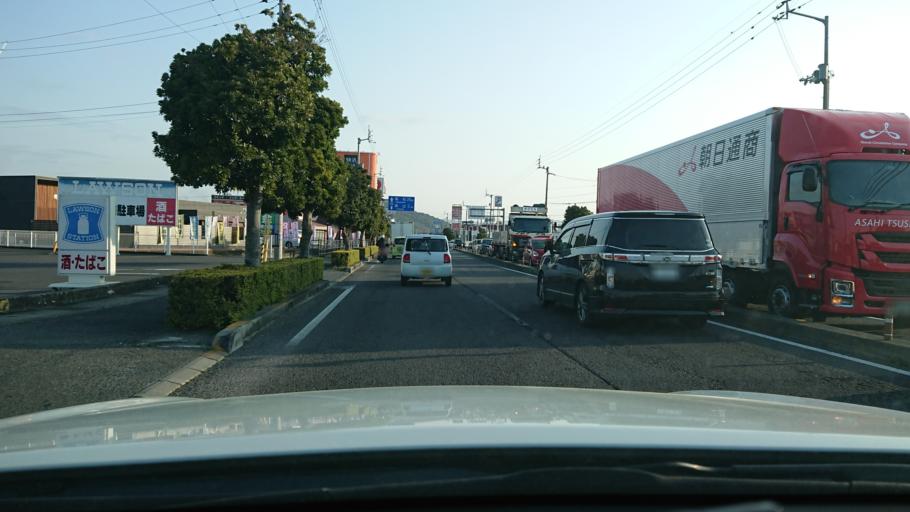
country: JP
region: Kagawa
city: Sakaidecho
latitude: 34.2905
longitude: 133.8322
